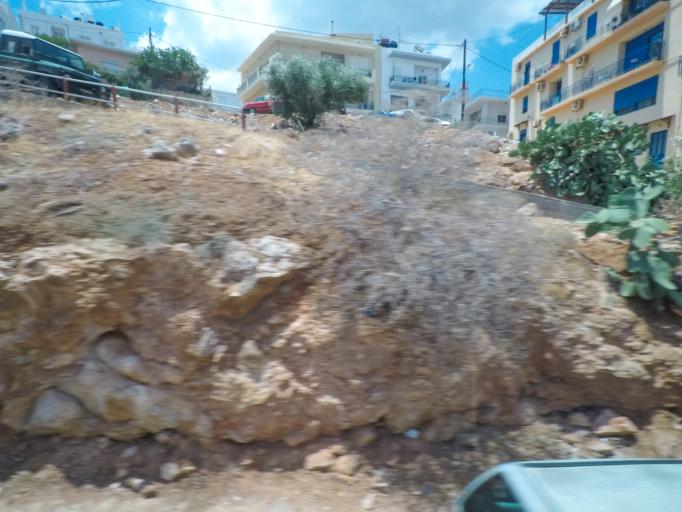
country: GR
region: Crete
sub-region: Nomos Lasithiou
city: Agios Nikolaos
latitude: 35.1909
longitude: 25.7216
